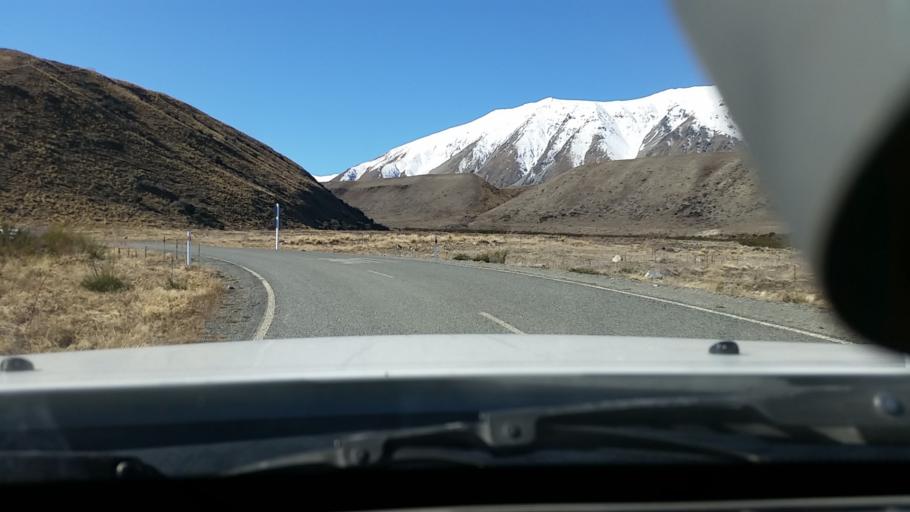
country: NZ
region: Canterbury
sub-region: Timaru District
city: Pleasant Point
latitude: -43.9120
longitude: 170.5598
